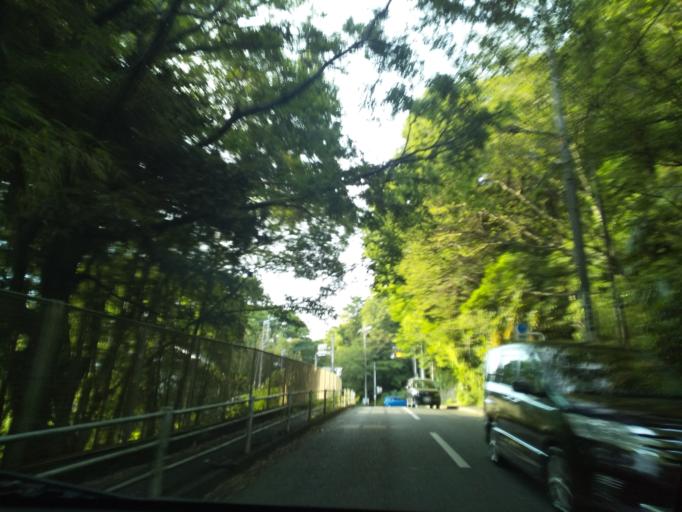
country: JP
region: Kanagawa
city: Zama
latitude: 35.5182
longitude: 139.3854
